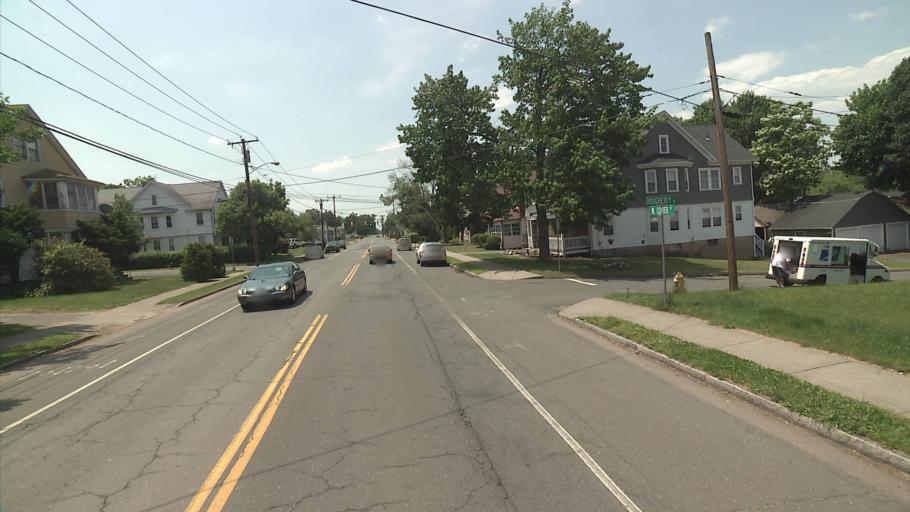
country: US
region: Connecticut
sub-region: Hartford County
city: Manchester
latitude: 41.7712
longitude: -72.5420
